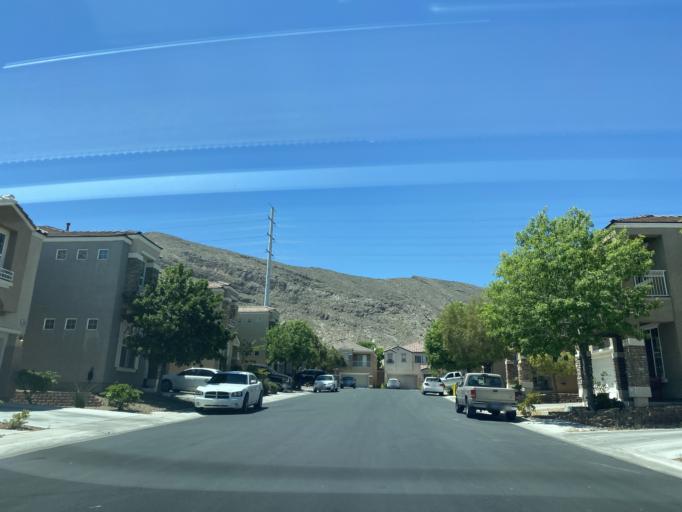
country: US
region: Nevada
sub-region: Clark County
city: Summerlin South
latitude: 36.2286
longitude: -115.3285
